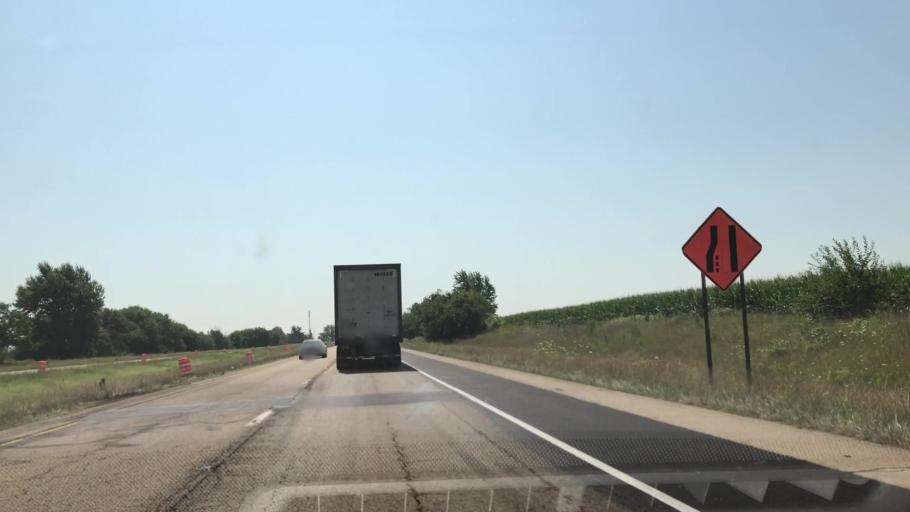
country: US
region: Illinois
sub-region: McLean County
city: Danvers
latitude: 40.6026
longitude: -89.1720
